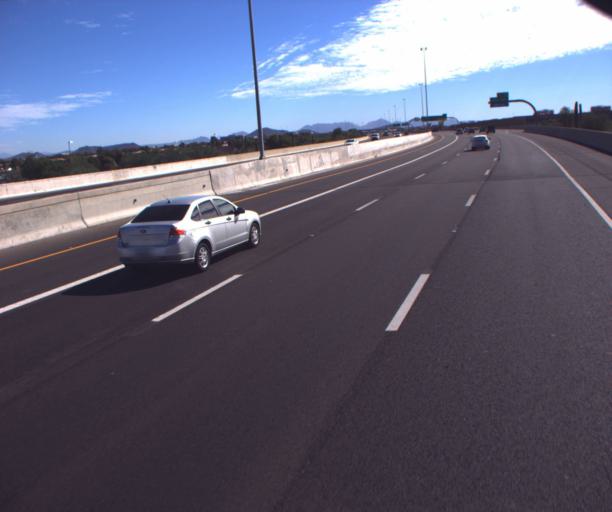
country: US
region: Arizona
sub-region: Maricopa County
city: Peoria
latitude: 33.6690
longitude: -112.1346
